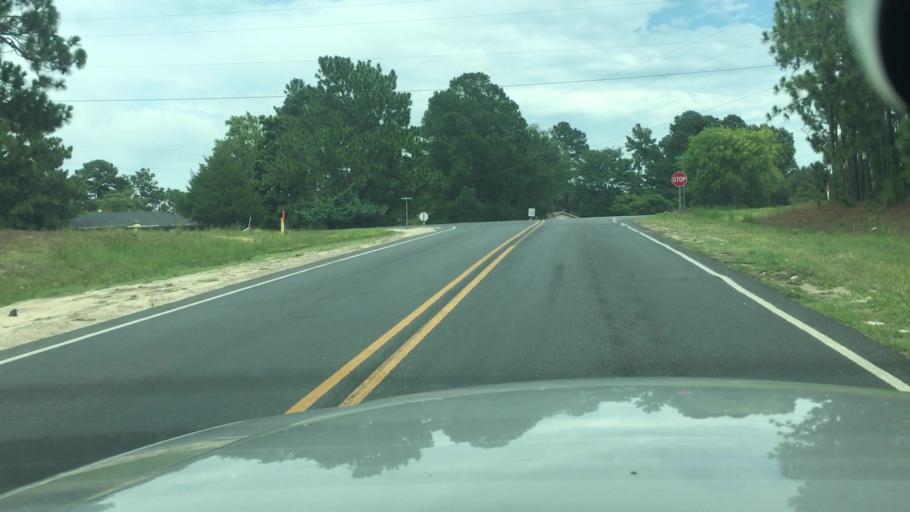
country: US
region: North Carolina
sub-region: Cumberland County
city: Hope Mills
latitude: 34.9640
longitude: -78.8932
